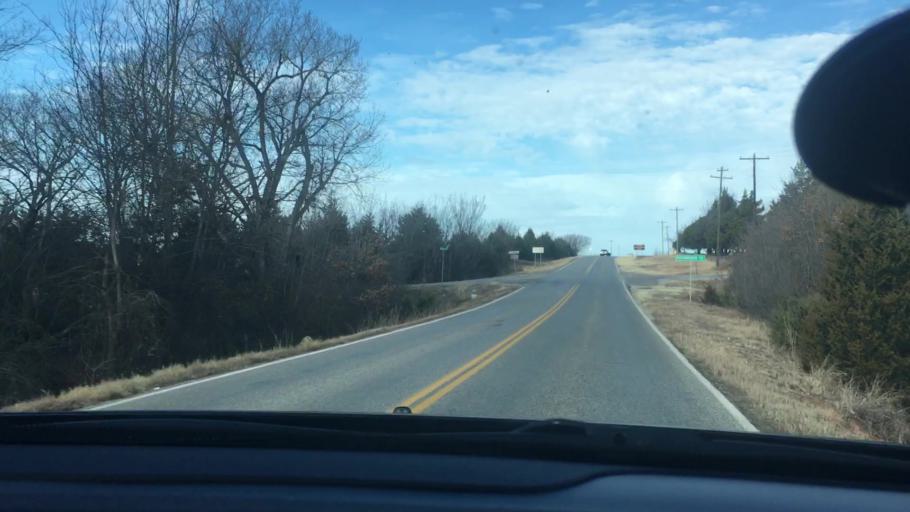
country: US
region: Oklahoma
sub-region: Seminole County
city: Konawa
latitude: 34.9688
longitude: -96.7746
